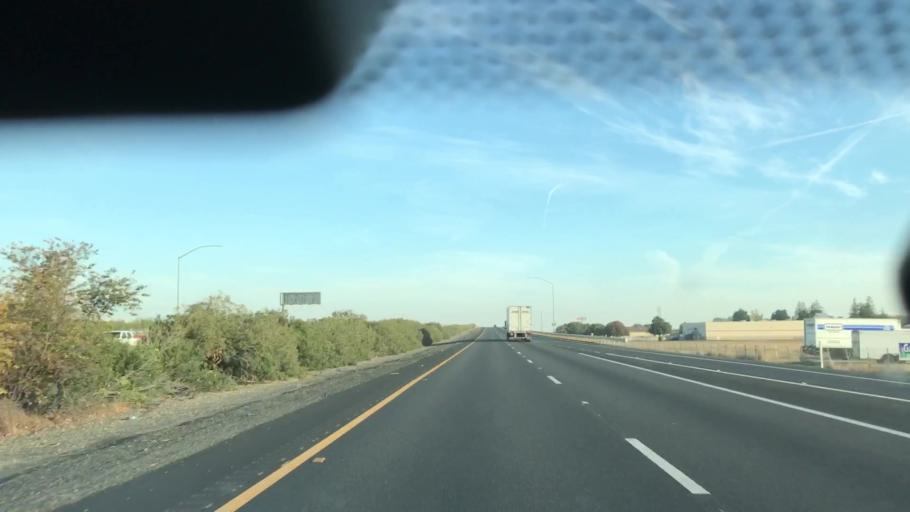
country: US
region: California
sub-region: Glenn County
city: Willows
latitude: 39.5263
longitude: -122.2146
